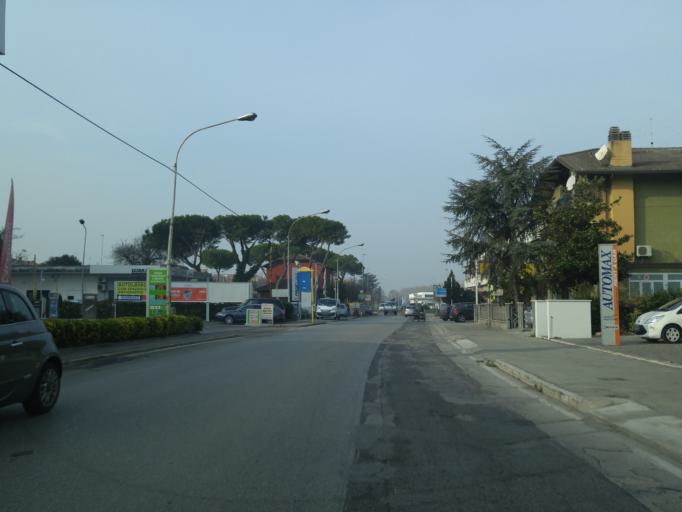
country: IT
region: Emilia-Romagna
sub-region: Provincia di Rimini
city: Cattolica
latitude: 43.9642
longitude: 12.7258
